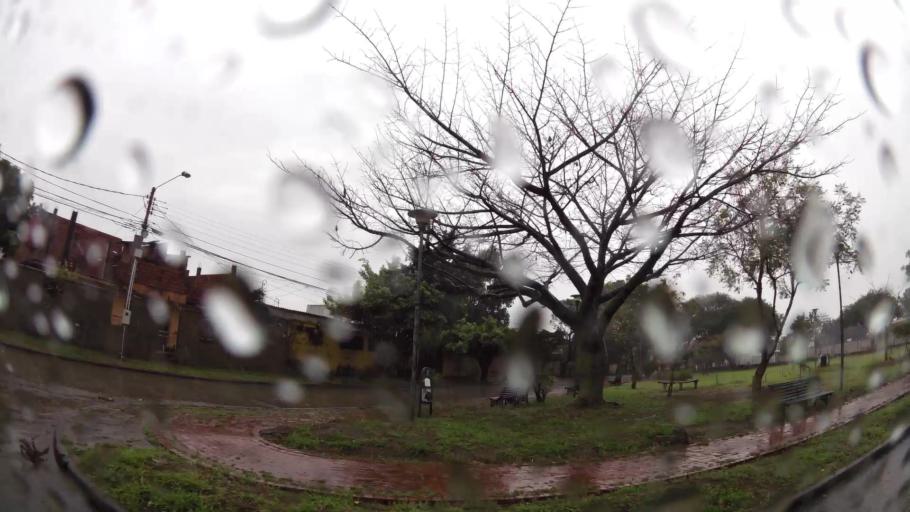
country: BO
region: Santa Cruz
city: Santa Cruz de la Sierra
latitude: -17.8019
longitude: -63.1644
